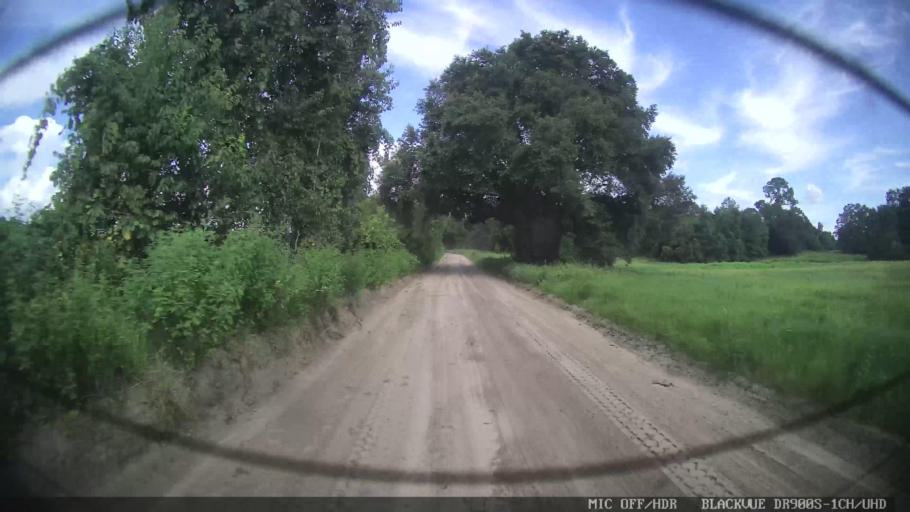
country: US
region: Florida
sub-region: Madison County
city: Madison
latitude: 30.5848
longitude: -83.2234
